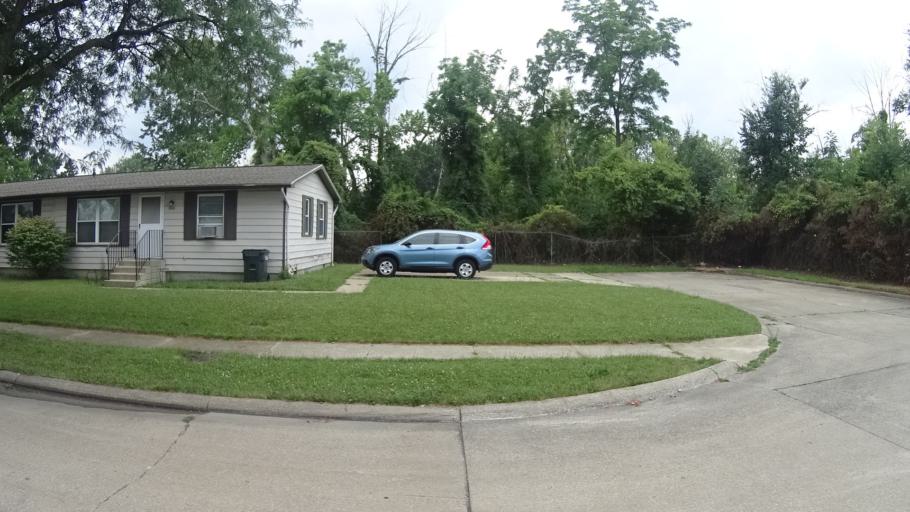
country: US
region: Ohio
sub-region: Erie County
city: Sandusky
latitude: 41.4392
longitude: -82.7377
